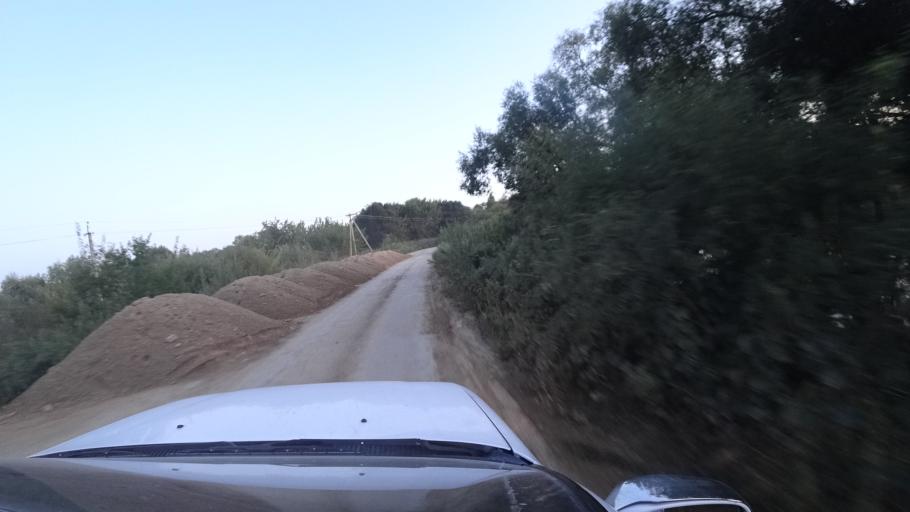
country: RU
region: Primorskiy
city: Dal'nerechensk
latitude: 45.9376
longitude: 133.7601
